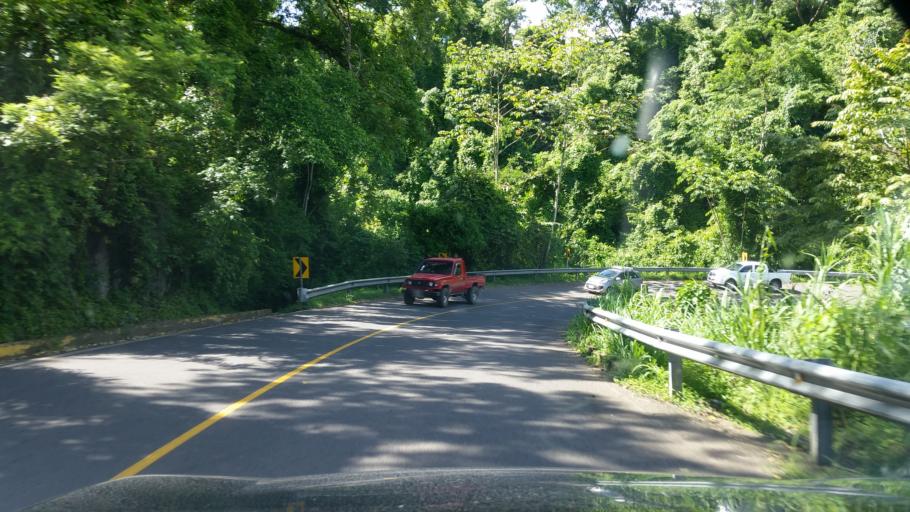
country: NI
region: Matagalpa
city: San Ramon
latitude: 13.0223
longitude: -85.7908
